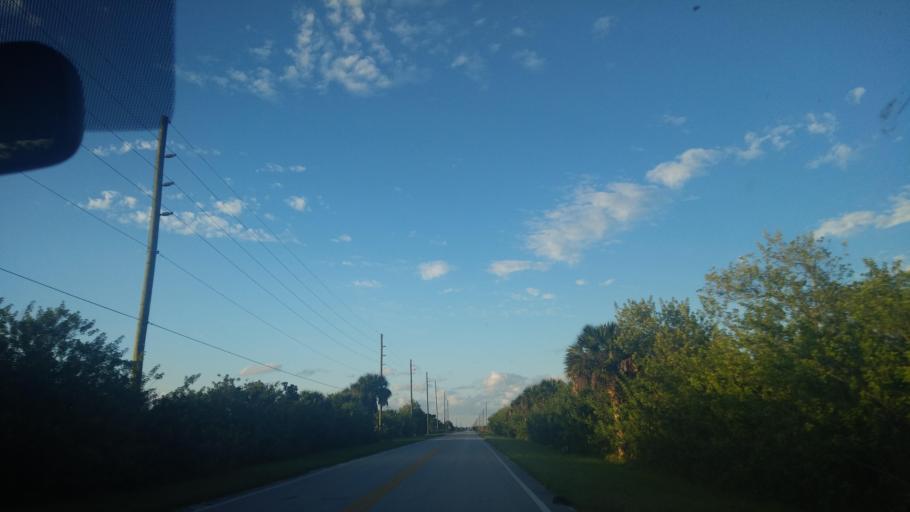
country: US
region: Florida
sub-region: Indian River County
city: Fellsmere
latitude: 27.6968
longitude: -80.6429
